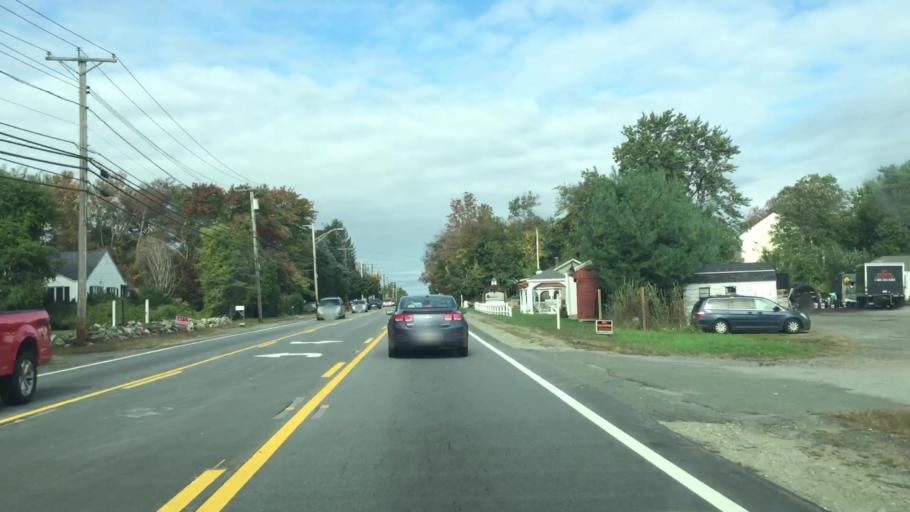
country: US
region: Massachusetts
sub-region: Essex County
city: Andover
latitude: 42.6632
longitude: -71.1120
